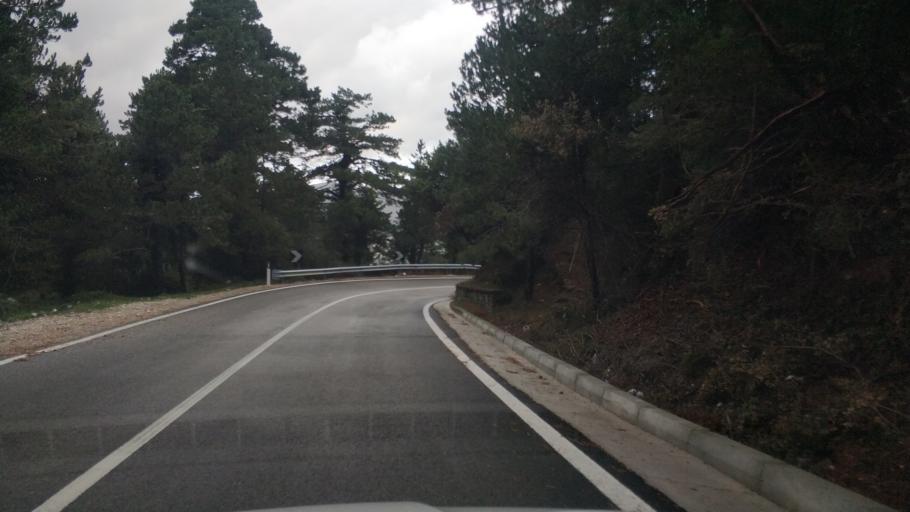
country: AL
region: Vlore
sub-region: Rrethi i Vlores
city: Brataj
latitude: 40.2184
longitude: 19.5791
